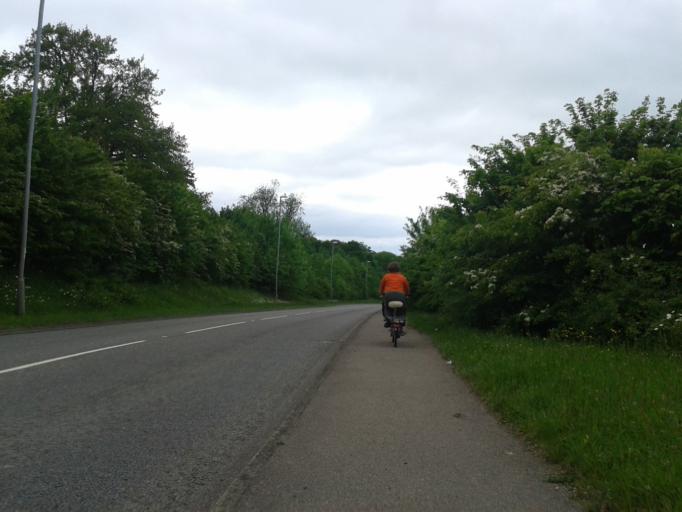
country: GB
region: England
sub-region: Cambridgeshire
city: Great Stukeley
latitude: 52.3716
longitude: -0.2474
